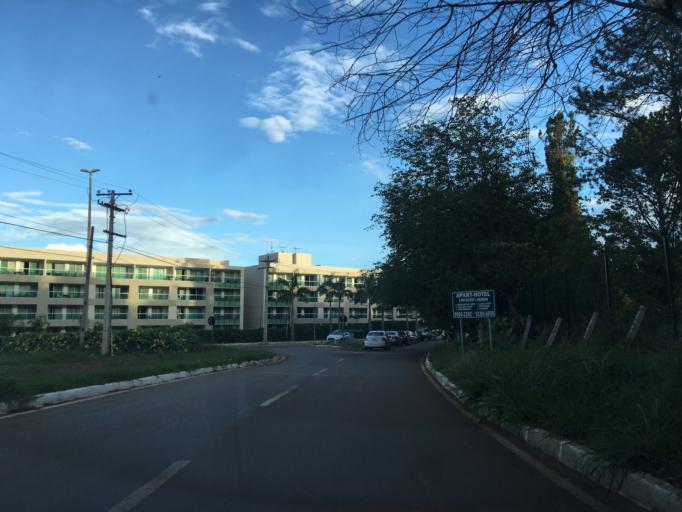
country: BR
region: Federal District
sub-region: Brasilia
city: Brasilia
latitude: -15.8060
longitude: -47.8318
